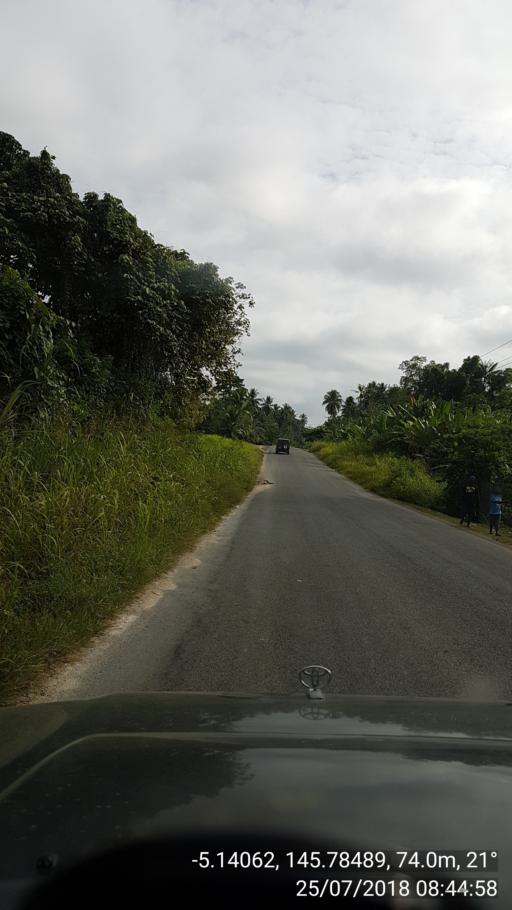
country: PG
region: Madang
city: Madang
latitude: -5.1406
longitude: 145.7848
